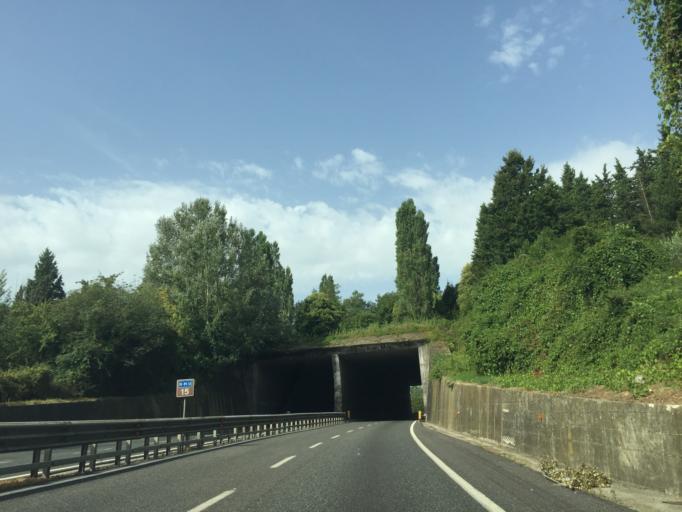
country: IT
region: Tuscany
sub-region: Province of Pisa
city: San Romano
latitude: 43.6872
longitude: 10.7770
